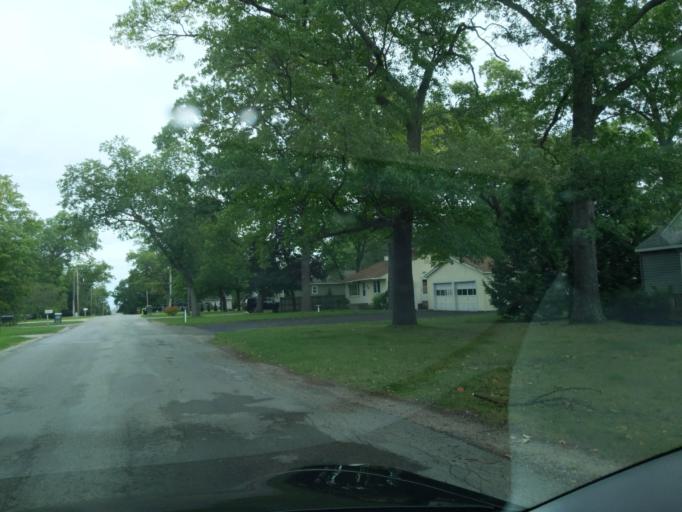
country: US
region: Michigan
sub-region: Grand Traverse County
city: Traverse City
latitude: 44.7499
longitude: -85.5714
